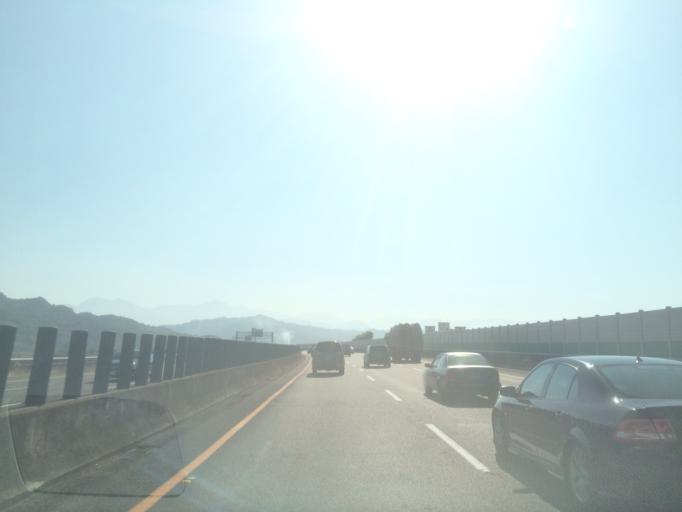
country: TW
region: Taiwan
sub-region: Nantou
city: Nantou
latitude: 23.9159
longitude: 120.6917
